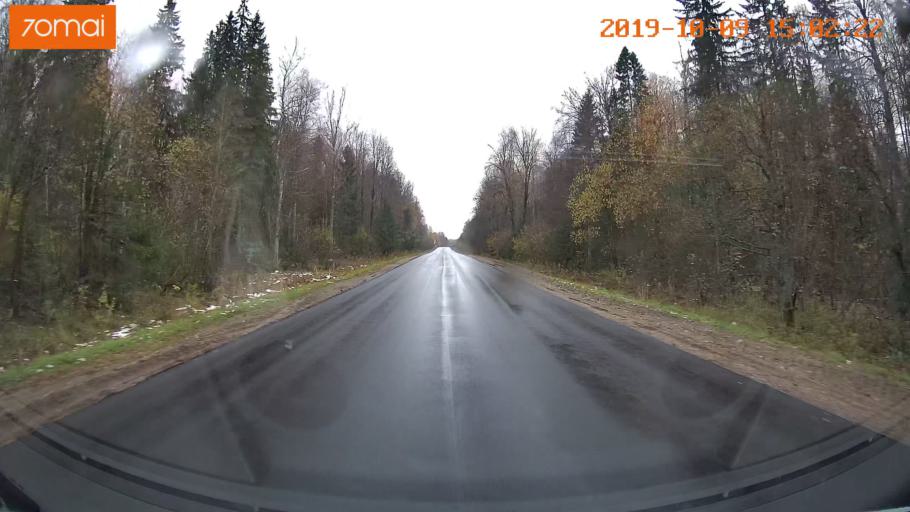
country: RU
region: Kostroma
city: Chistyye Bory
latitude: 58.2862
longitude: 41.6793
